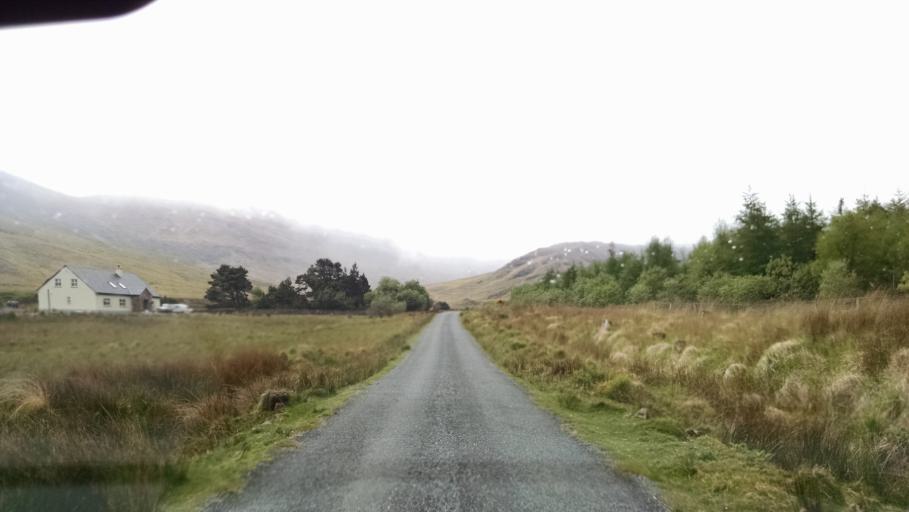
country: IE
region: Connaught
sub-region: Maigh Eo
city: Westport
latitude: 53.6464
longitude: -9.6658
